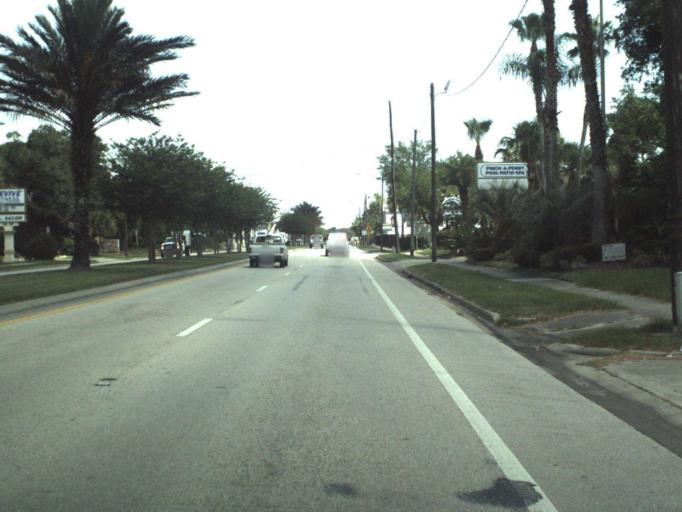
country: US
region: Florida
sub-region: Volusia County
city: Ormond Beach
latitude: 29.2780
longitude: -81.0594
